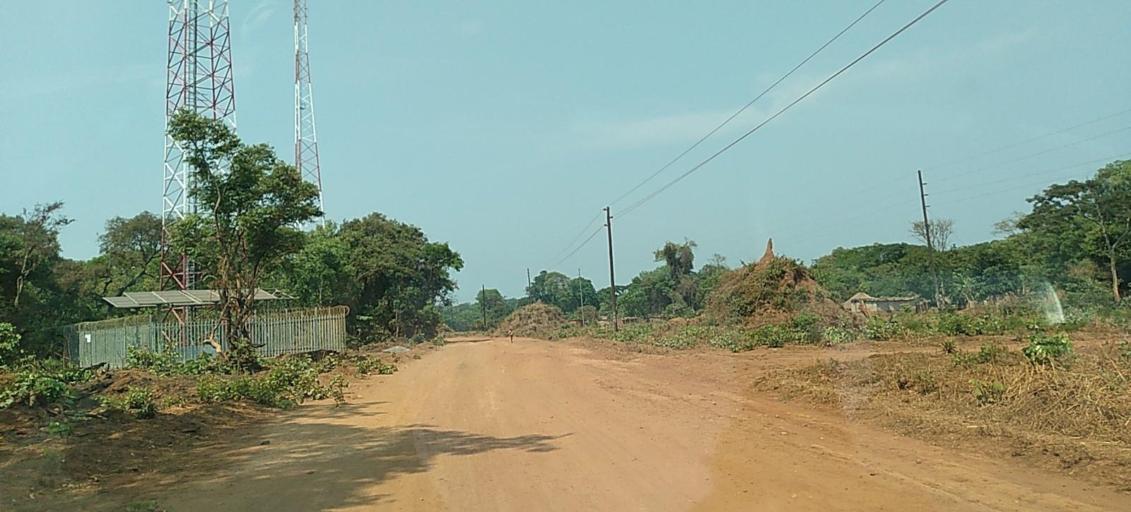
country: ZM
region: Copperbelt
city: Chingola
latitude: -13.0459
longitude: 27.4336
